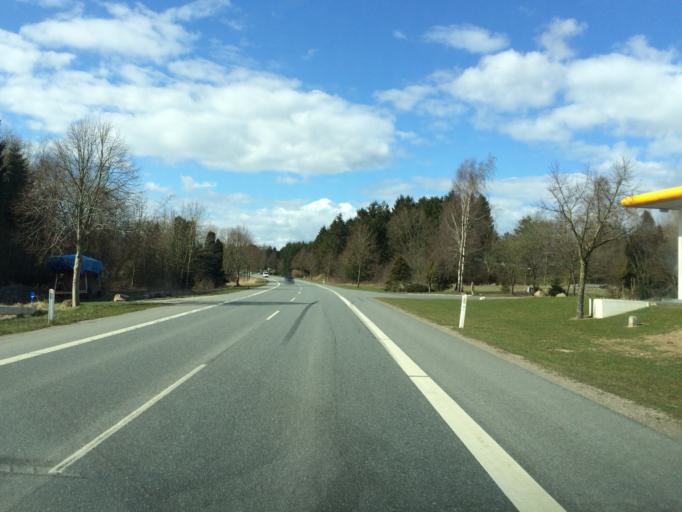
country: DK
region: South Denmark
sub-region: Assens Kommune
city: Arup
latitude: 55.4047
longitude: 10.0834
